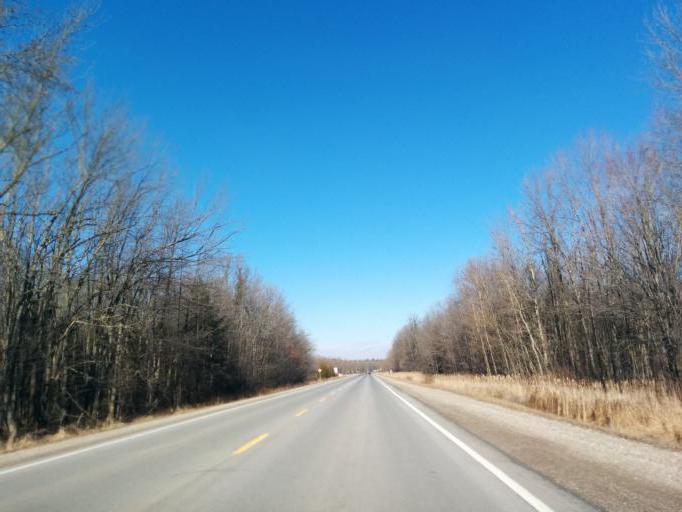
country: CA
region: Ontario
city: Brant
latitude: 43.0475
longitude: -80.3679
